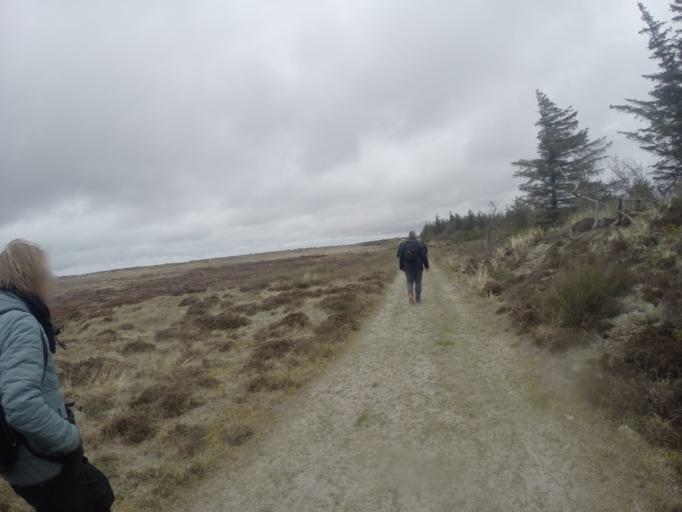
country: DK
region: North Denmark
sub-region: Thisted Kommune
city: Hurup
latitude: 56.9029
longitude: 8.3416
